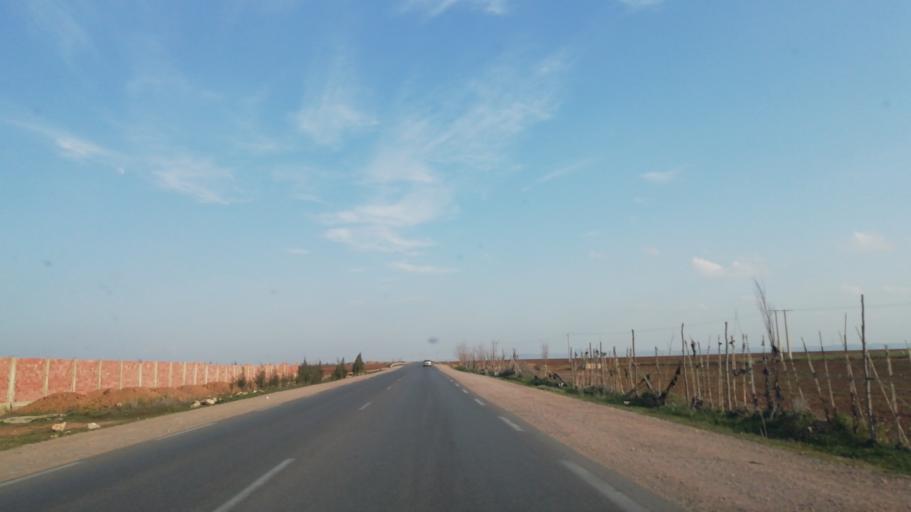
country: DZ
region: Relizane
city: Relizane
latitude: 35.8926
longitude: 0.6157
